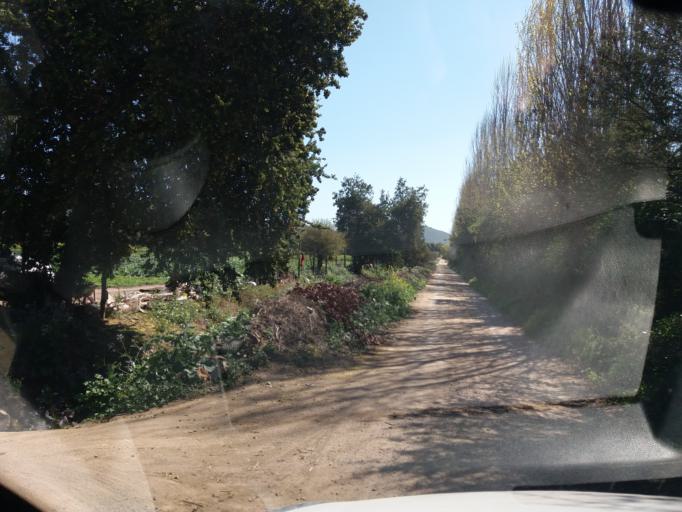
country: CL
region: Valparaiso
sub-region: Provincia de Quillota
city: Quillota
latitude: -32.9452
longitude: -71.2909
